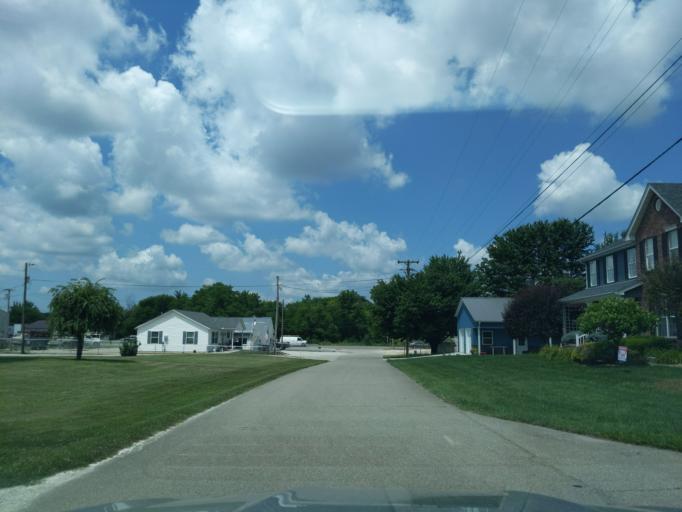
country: US
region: Indiana
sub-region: Ripley County
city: Osgood
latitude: 39.2027
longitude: -85.3292
